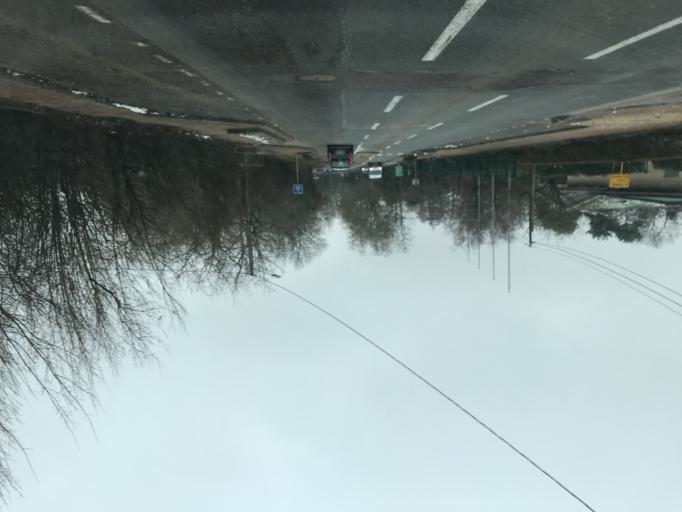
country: FR
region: Rhone-Alpes
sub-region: Departement de l'Ain
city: Villars-les-Dombes
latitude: 45.9958
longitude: 5.0275
